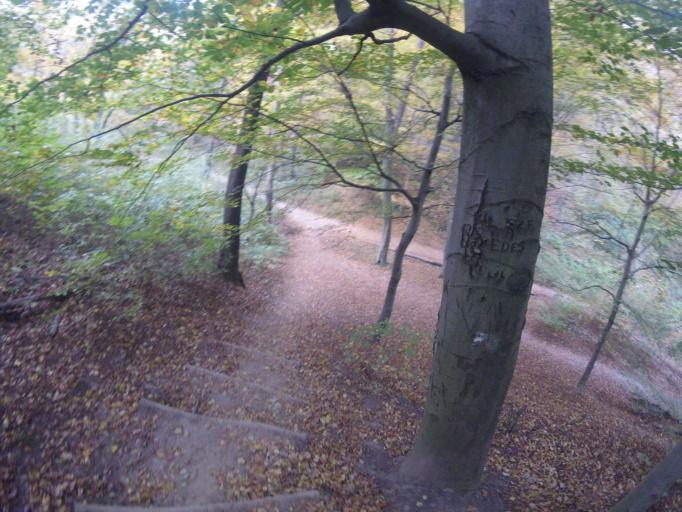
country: HU
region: Fejer
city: Bodajk
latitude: 47.3062
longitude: 18.2264
